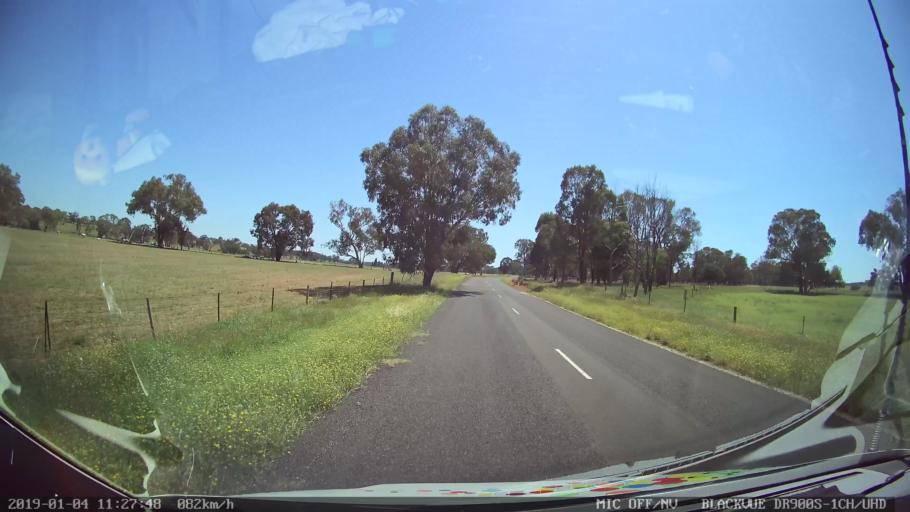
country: AU
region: New South Wales
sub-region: Cabonne
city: Molong
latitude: -33.1059
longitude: 148.7663
